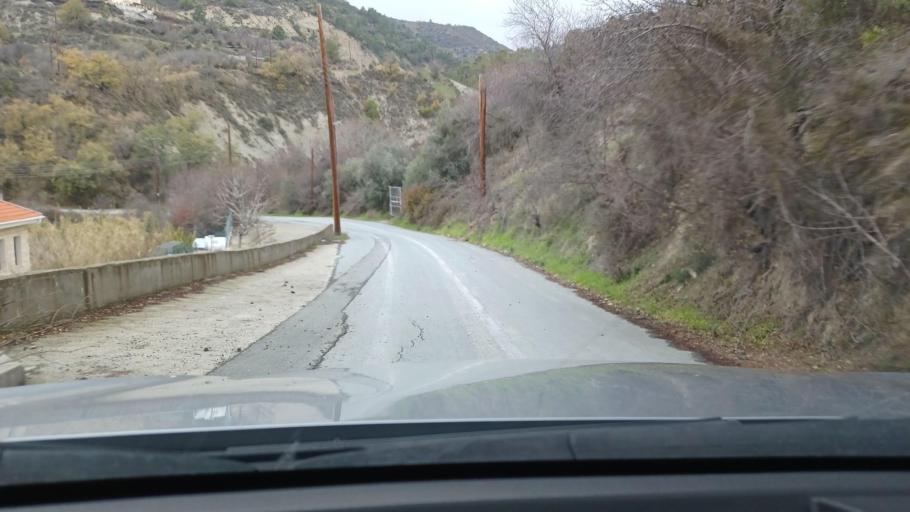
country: CY
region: Limassol
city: Pelendri
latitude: 34.8200
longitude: 32.8967
